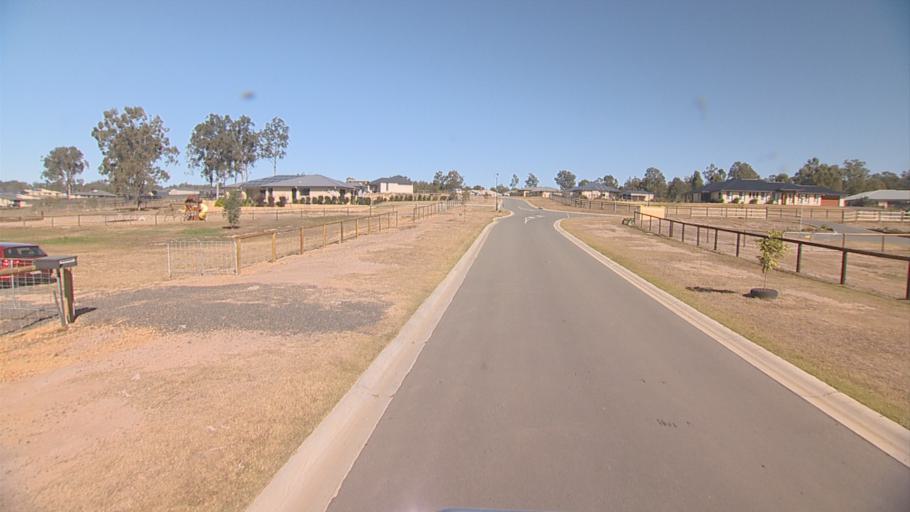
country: AU
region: Queensland
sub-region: Logan
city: Cedar Vale
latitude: -27.8658
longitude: 153.0432
